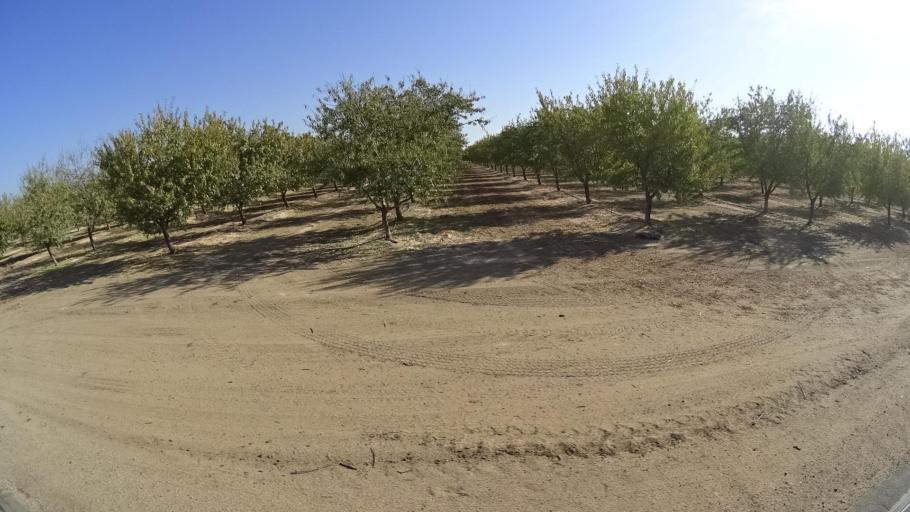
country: US
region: California
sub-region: Kern County
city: Delano
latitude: 35.7381
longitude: -119.2231
